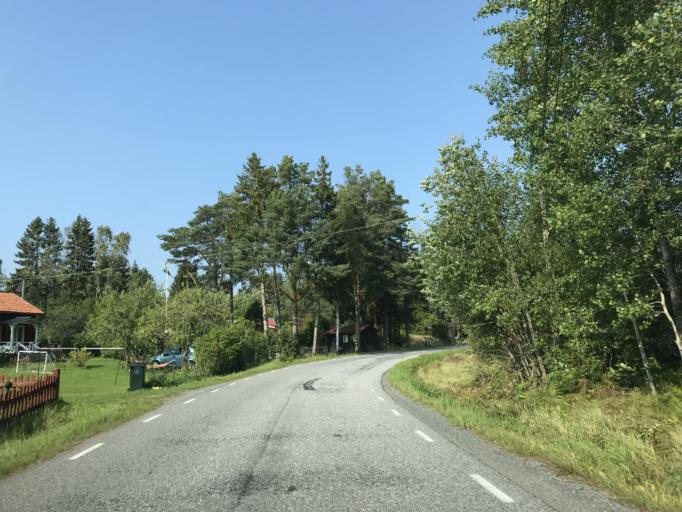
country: SE
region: Stockholm
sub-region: Norrtalje Kommun
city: Bjorko
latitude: 59.8681
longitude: 19.0481
